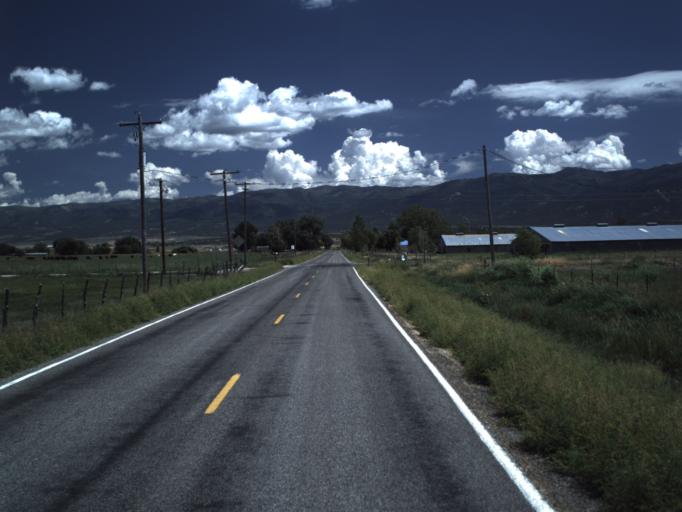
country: US
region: Utah
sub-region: Sanpete County
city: Moroni
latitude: 39.4759
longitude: -111.5736
